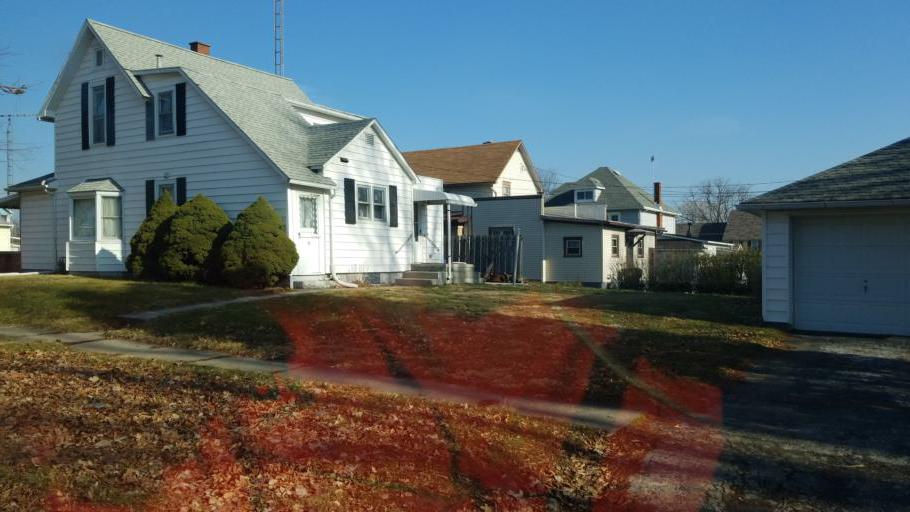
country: US
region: Ohio
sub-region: Seneca County
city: Tiffin
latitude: 41.1093
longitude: -83.1675
